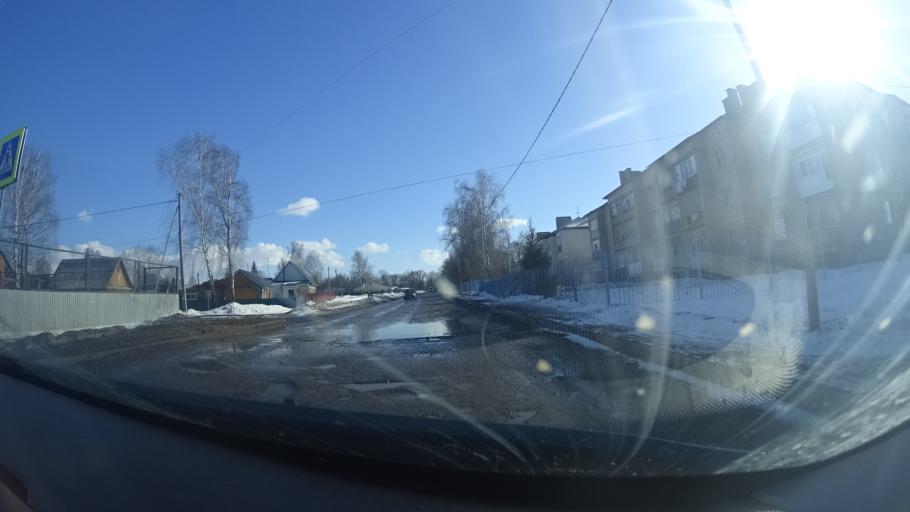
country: RU
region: Bashkortostan
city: Chishmy
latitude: 54.5869
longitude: 55.3702
